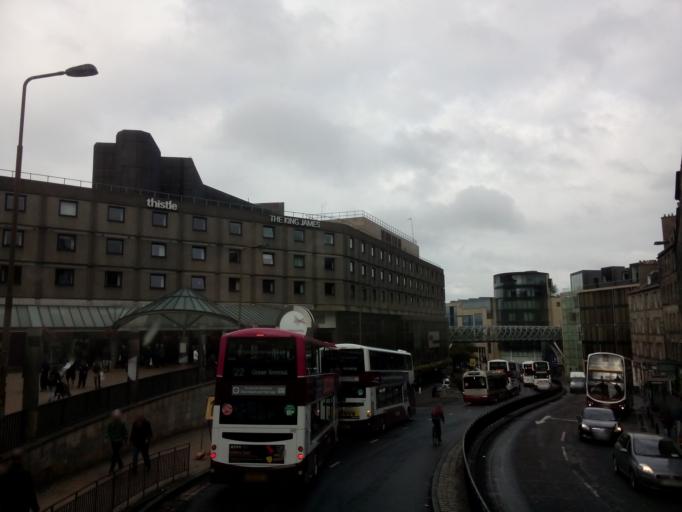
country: GB
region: Scotland
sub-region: Edinburgh
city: Edinburgh
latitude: 55.9537
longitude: -3.1887
